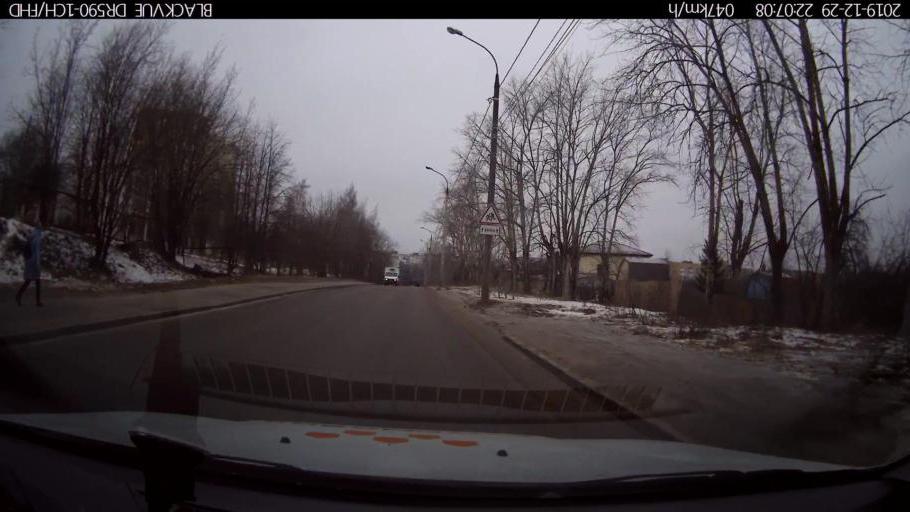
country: RU
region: Nizjnij Novgorod
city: Nizhniy Novgorod
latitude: 56.2262
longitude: 43.9509
